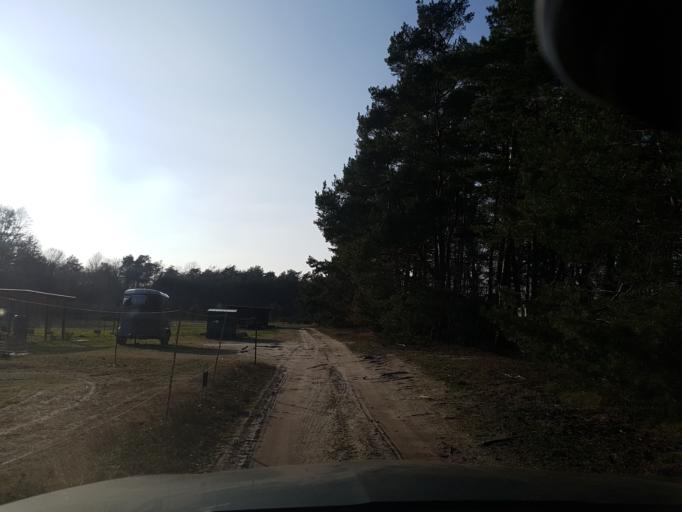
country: DE
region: Brandenburg
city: Schonewalde
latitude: 51.6346
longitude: 13.6148
